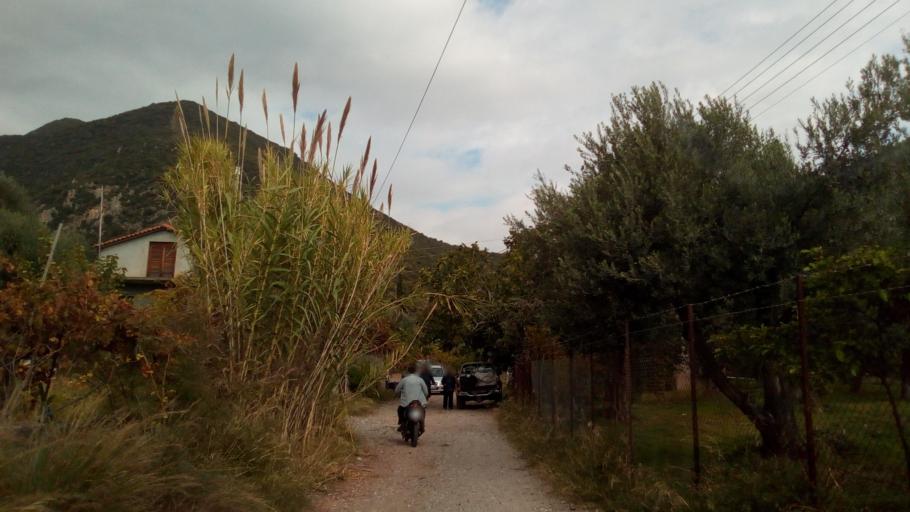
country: GR
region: West Greece
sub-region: Nomos Achaias
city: Kamarai
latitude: 38.3958
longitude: 22.0064
